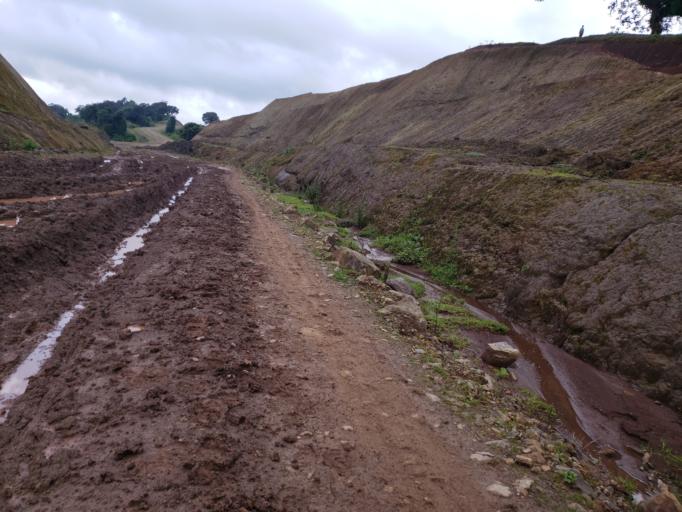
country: ET
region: Oromiya
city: Dodola
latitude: 6.6641
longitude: 39.3646
